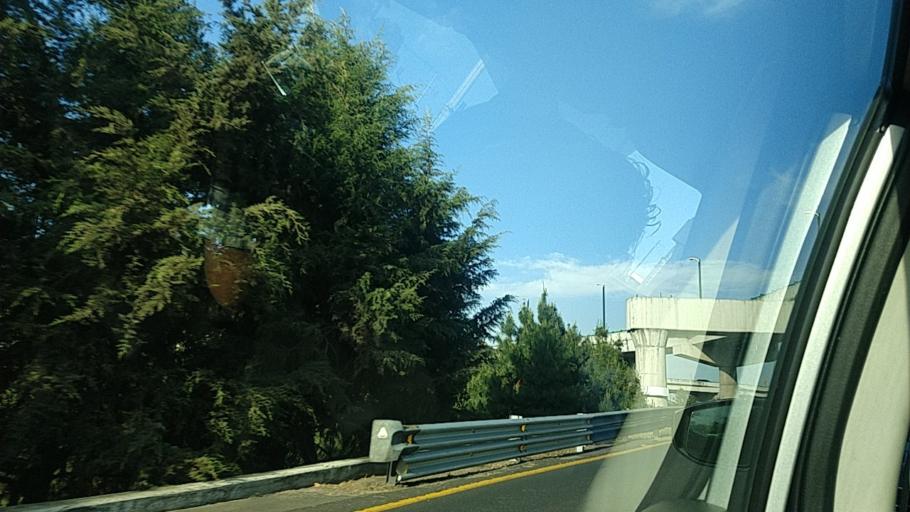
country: MX
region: Mexico
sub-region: San Mateo Atenco
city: Santa Maria la Asuncion
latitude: 19.2860
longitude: -99.5574
